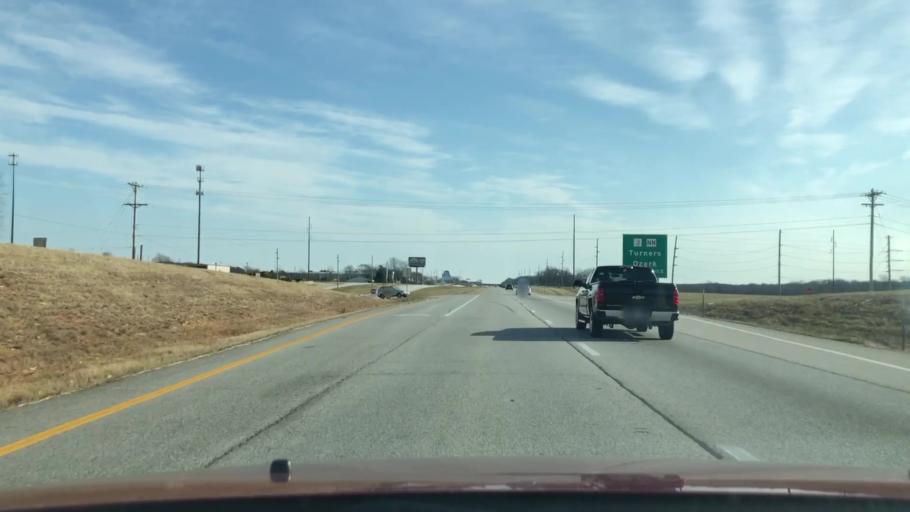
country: US
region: Missouri
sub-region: Christian County
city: Ozark
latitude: 37.1206
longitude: -93.2010
